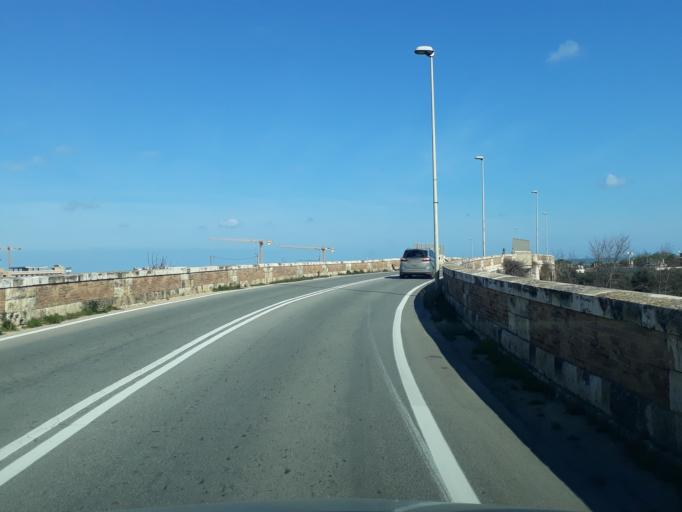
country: IT
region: Apulia
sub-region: Provincia di Bari
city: Monopoli
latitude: 40.9560
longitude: 17.2821
